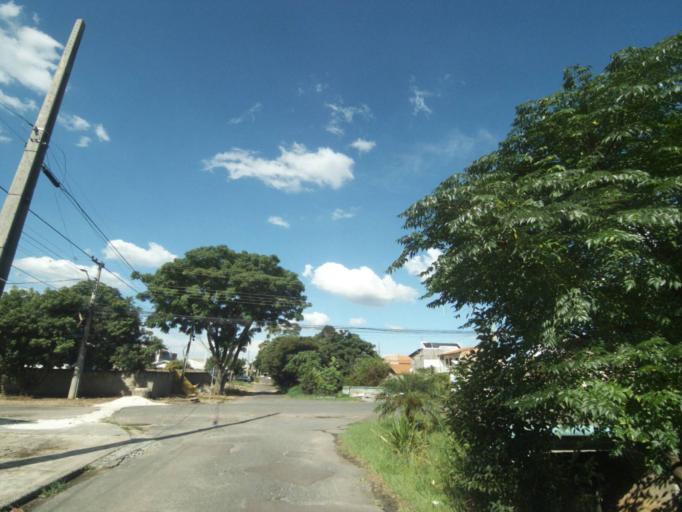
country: BR
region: Parana
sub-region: Pinhais
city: Pinhais
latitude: -25.4549
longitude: -49.2052
